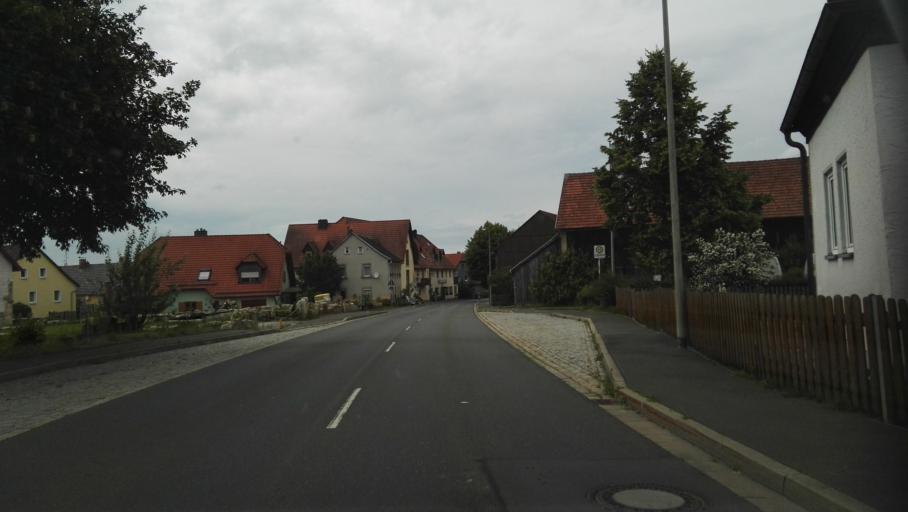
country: DE
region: Bavaria
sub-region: Upper Franconia
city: Plankenfels
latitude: 49.8829
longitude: 11.3349
